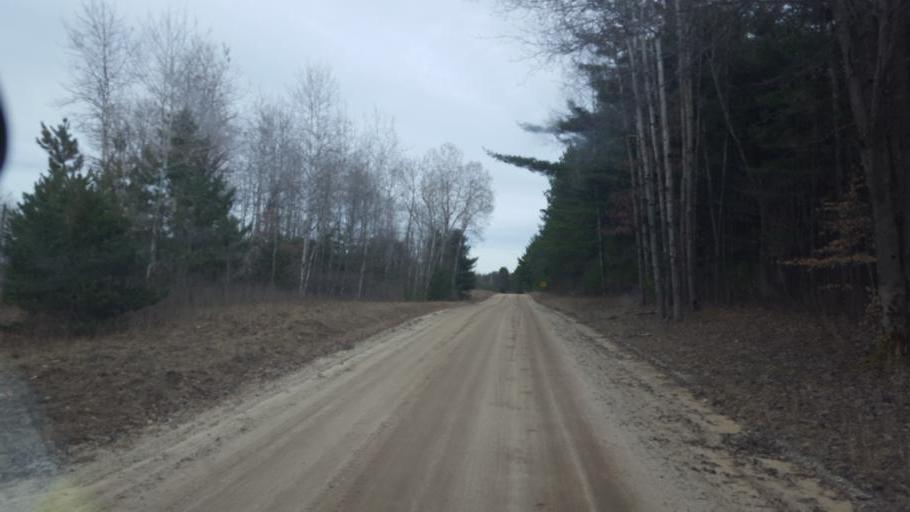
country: US
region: Michigan
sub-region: Montcalm County
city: Edmore
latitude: 43.5095
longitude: -85.0105
